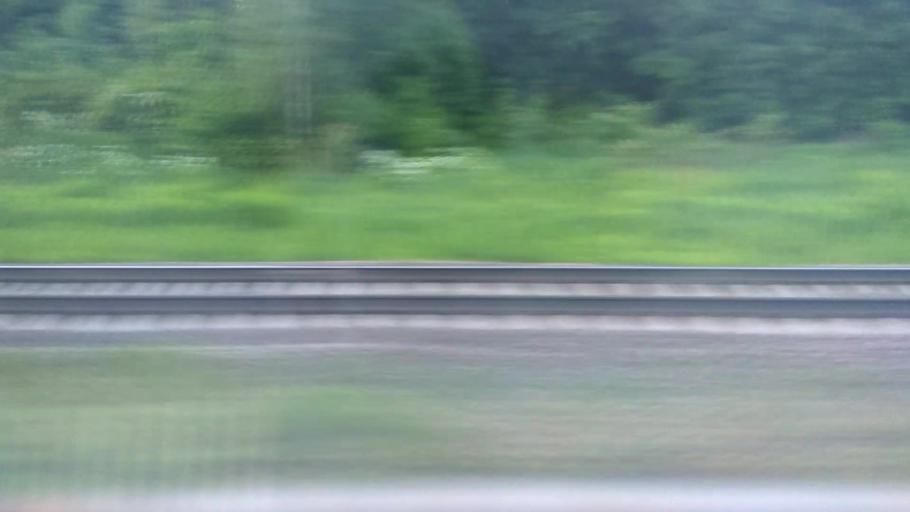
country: RU
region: Moskovskaya
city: Vostryakovo
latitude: 55.4022
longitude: 37.7999
